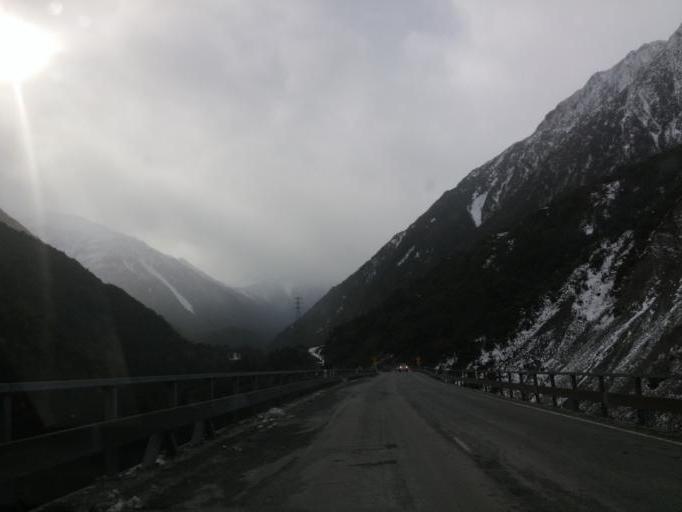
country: NZ
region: West Coast
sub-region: Grey District
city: Greymouth
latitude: -42.8867
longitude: 171.5554
